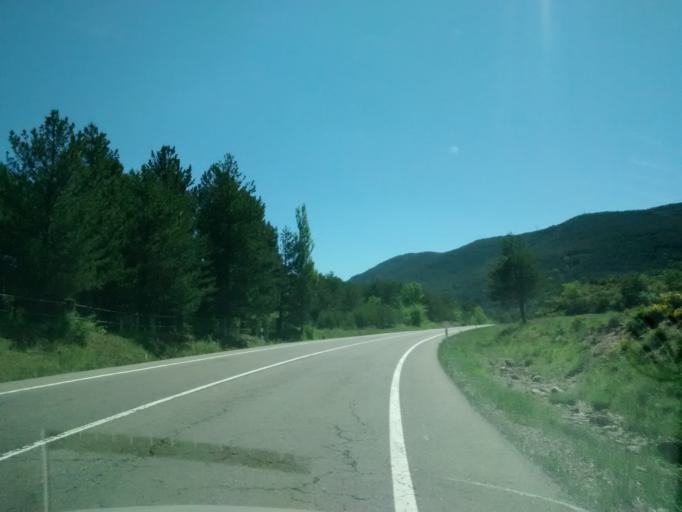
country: ES
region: Aragon
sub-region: Provincia de Huesca
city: Villanua
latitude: 42.6587
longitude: -0.5548
